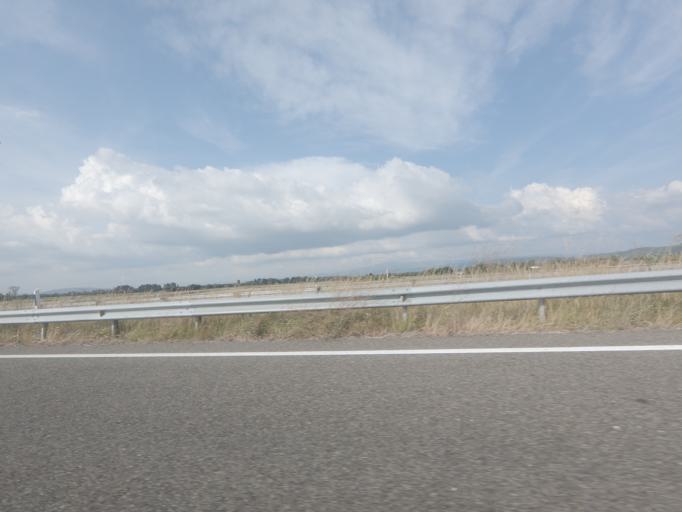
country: ES
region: Galicia
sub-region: Provincia de Ourense
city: Xinzo de Limia
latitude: 42.0882
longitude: -7.7208
